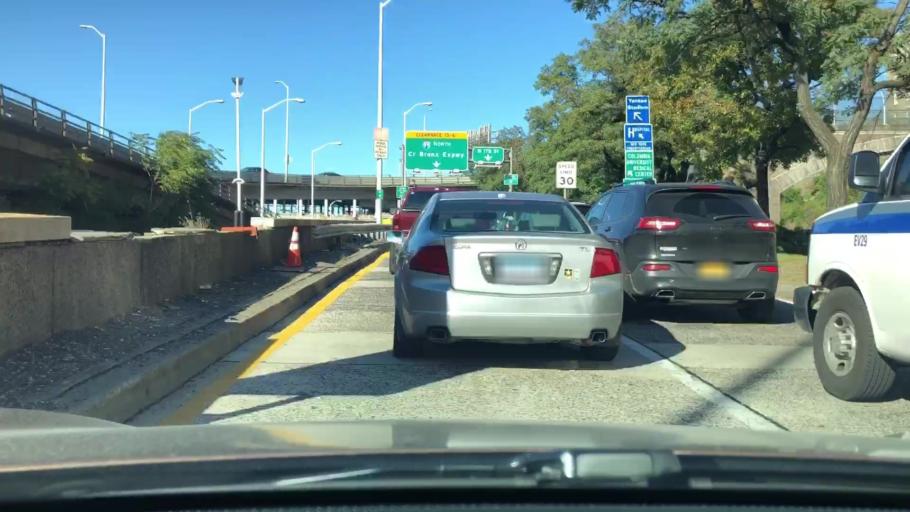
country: US
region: New York
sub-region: New York County
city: Inwood
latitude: 40.8473
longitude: -73.9430
